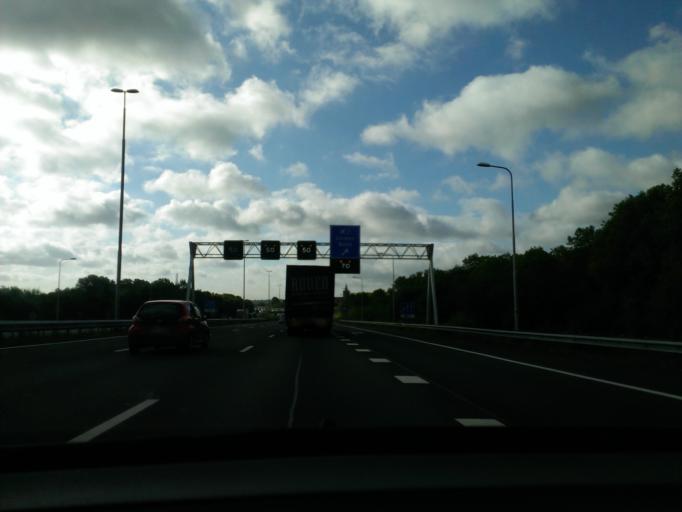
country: NL
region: Limburg
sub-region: Gemeente Beek
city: Beek
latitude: 50.9588
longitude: 5.8062
